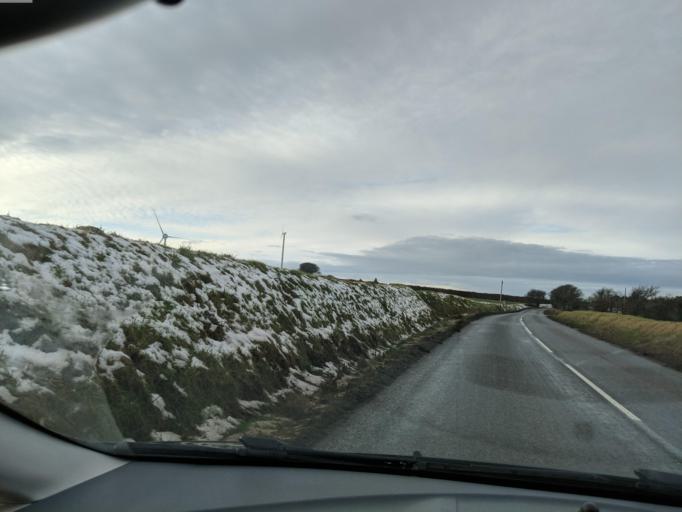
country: GB
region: England
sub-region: Cornwall
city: Jacobstow
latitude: 50.6643
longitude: -4.5901
